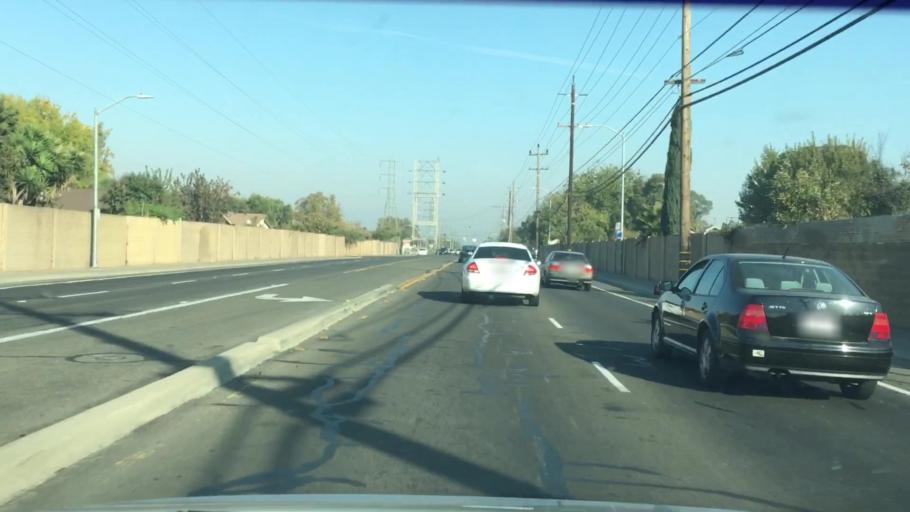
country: US
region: California
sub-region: Sacramento County
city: Florin
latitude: 38.4780
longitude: -121.4087
